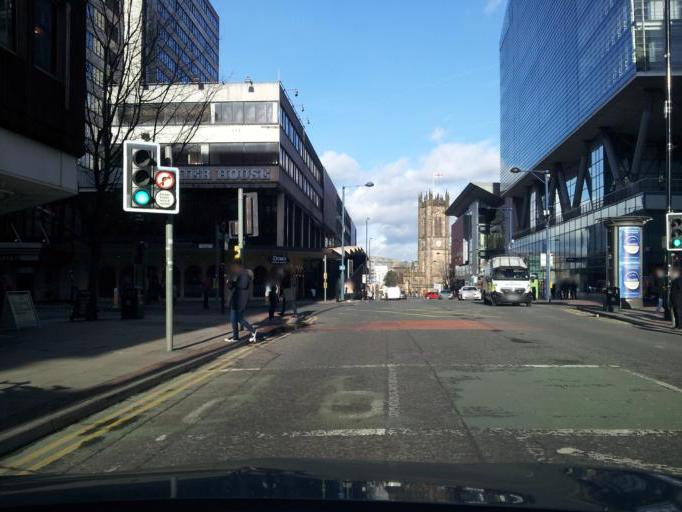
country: GB
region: England
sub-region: Manchester
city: Manchester
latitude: 53.4831
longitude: -2.2463
